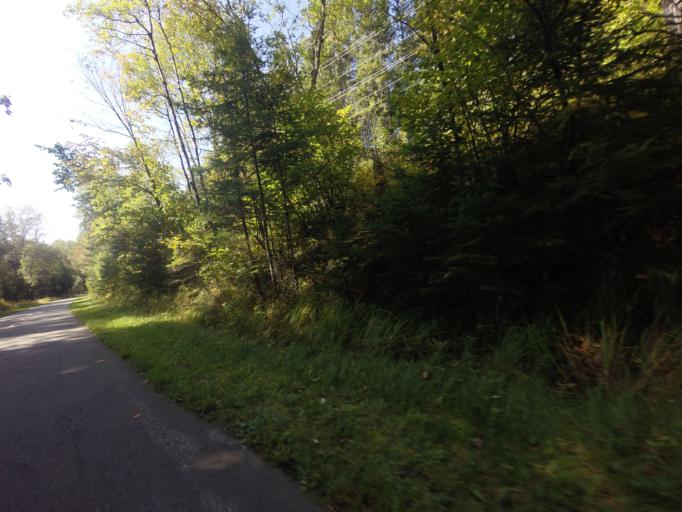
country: CA
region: Quebec
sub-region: Laurentides
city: Mont-Tremblant
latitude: 46.1269
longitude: -74.5678
